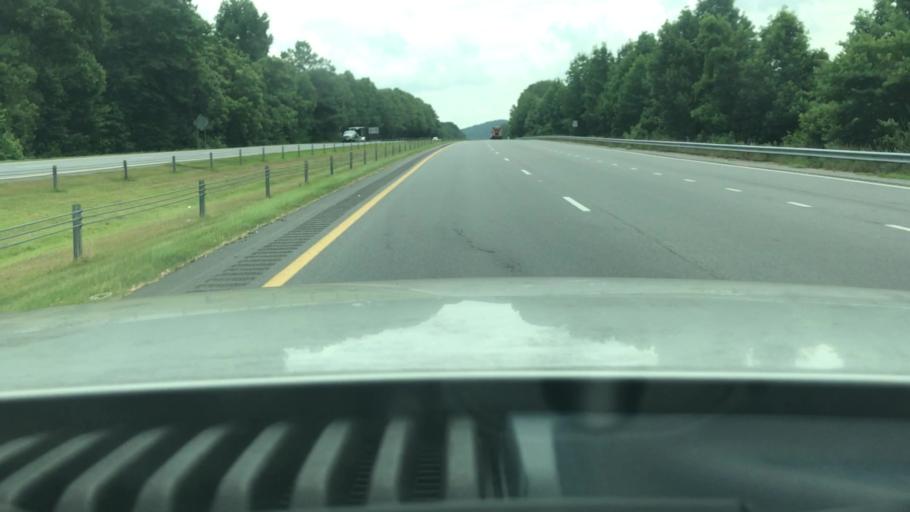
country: US
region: North Carolina
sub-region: Wilkes County
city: North Wilkesboro
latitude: 36.1368
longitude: -81.1025
